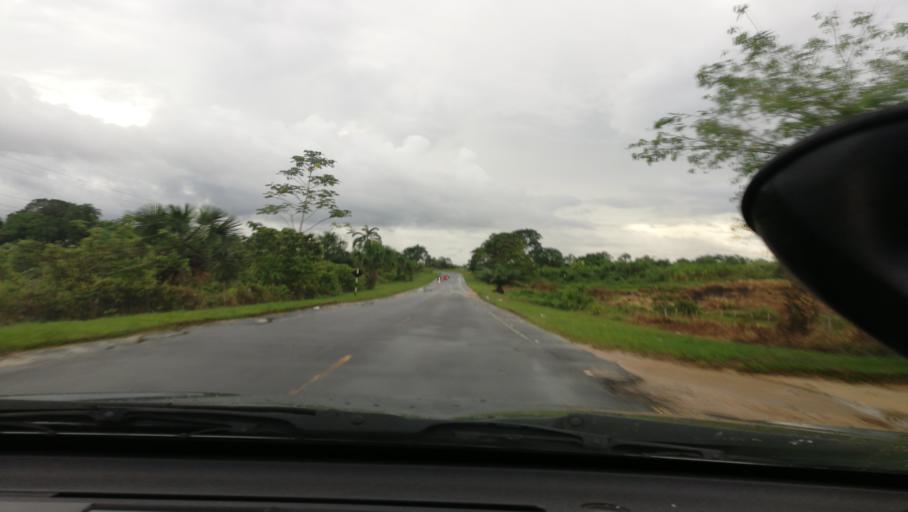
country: PE
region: Loreto
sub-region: Provincia de Maynas
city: Iquitos
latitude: -3.9174
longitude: -73.3662
